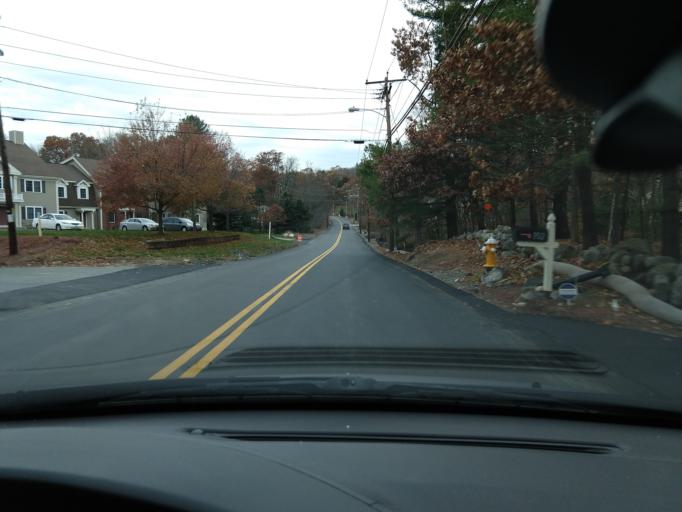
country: US
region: Massachusetts
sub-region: Middlesex County
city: Westford
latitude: 42.5860
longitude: -71.4265
